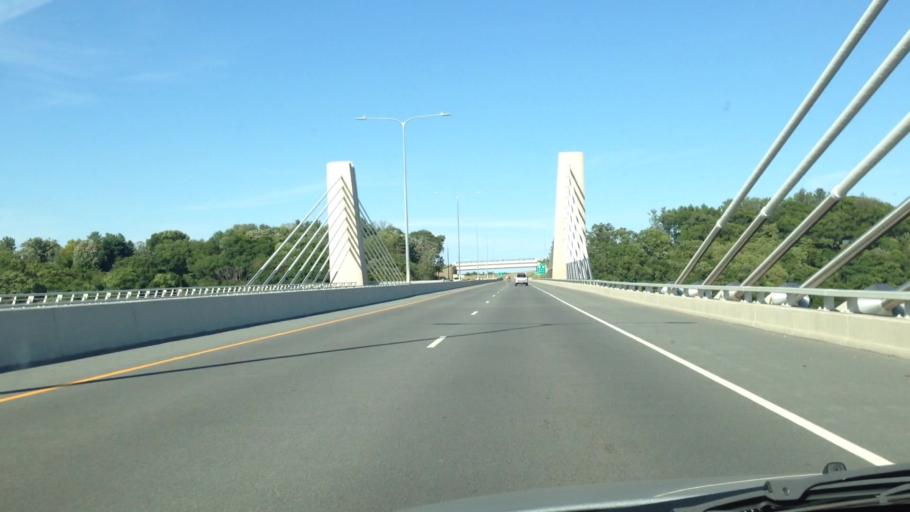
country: US
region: Minnesota
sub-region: Washington County
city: Oak Park Heights
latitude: 45.0425
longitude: -92.7814
